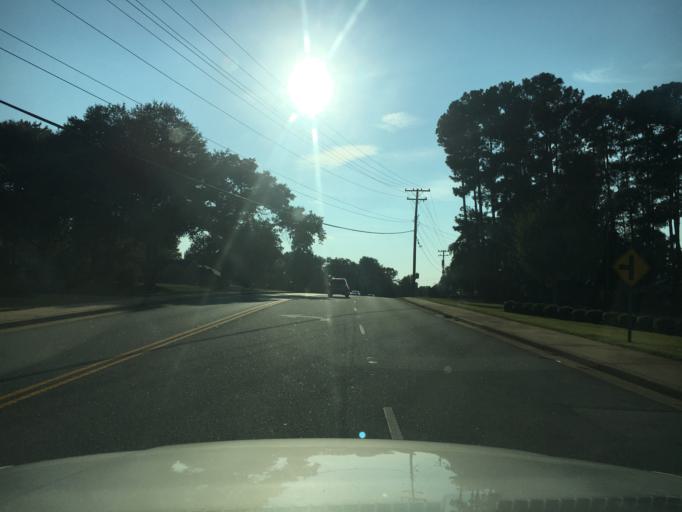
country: US
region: South Carolina
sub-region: Greenville County
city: Taylors
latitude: 34.8906
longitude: -82.2764
